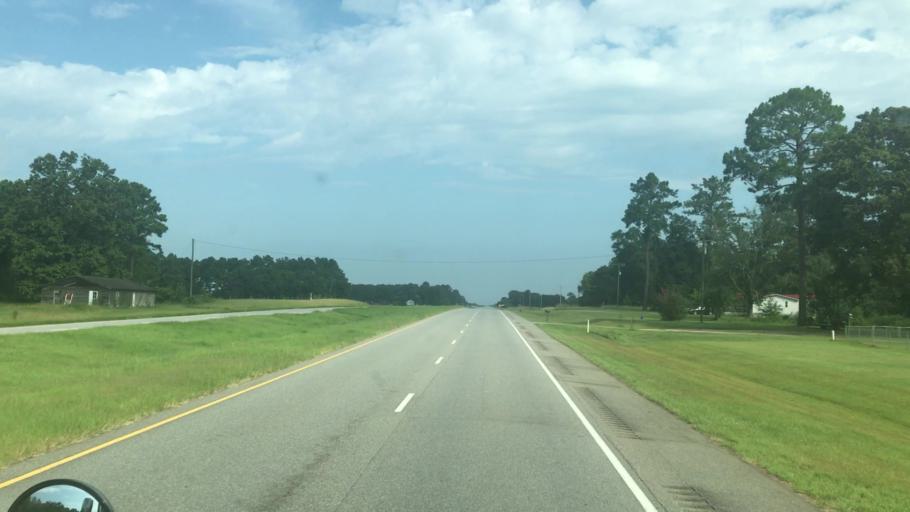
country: US
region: Georgia
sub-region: Early County
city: Blakely
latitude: 31.3119
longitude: -84.8726
